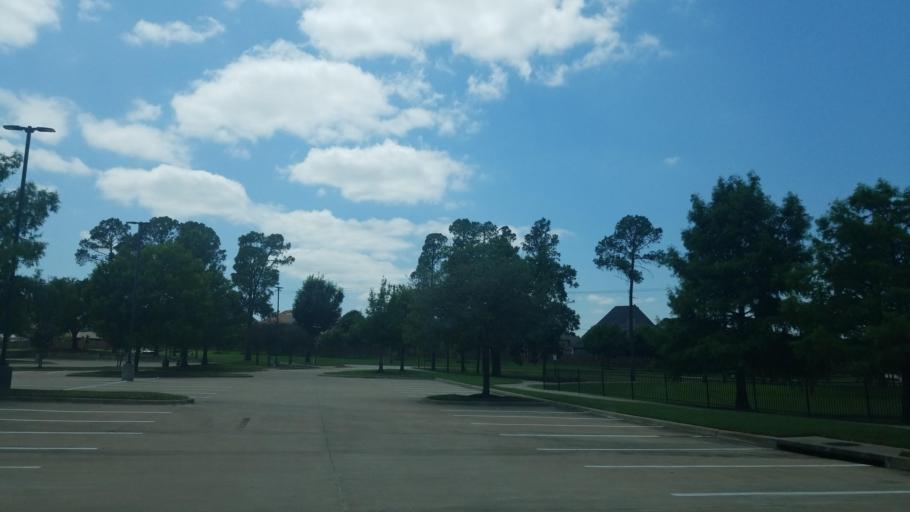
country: US
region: Texas
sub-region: Denton County
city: Copper Canyon
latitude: 33.0759
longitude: -97.0861
